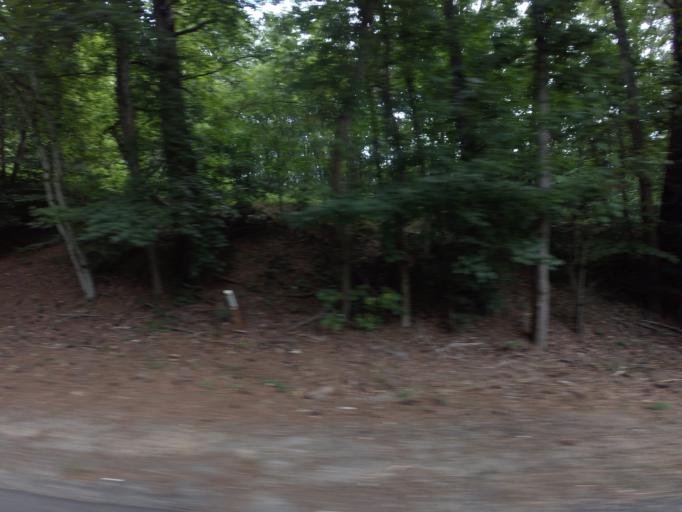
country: US
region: Georgia
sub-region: Fulton County
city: Johns Creek
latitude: 34.0308
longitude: -84.1689
